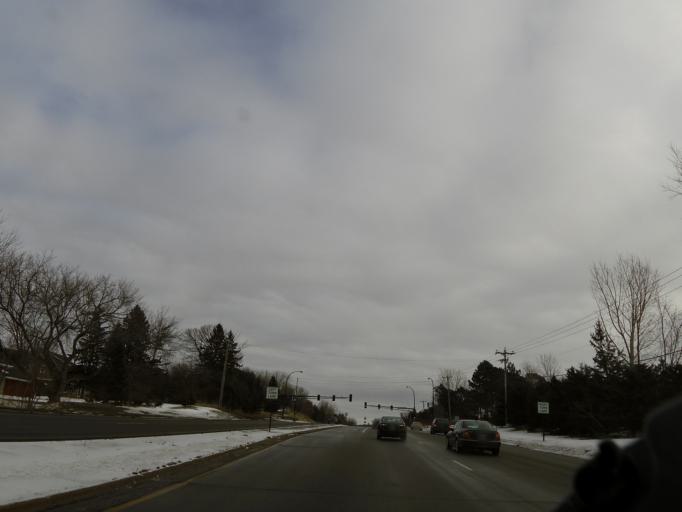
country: US
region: Minnesota
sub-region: Washington County
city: Woodbury
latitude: 44.9198
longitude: -92.9192
